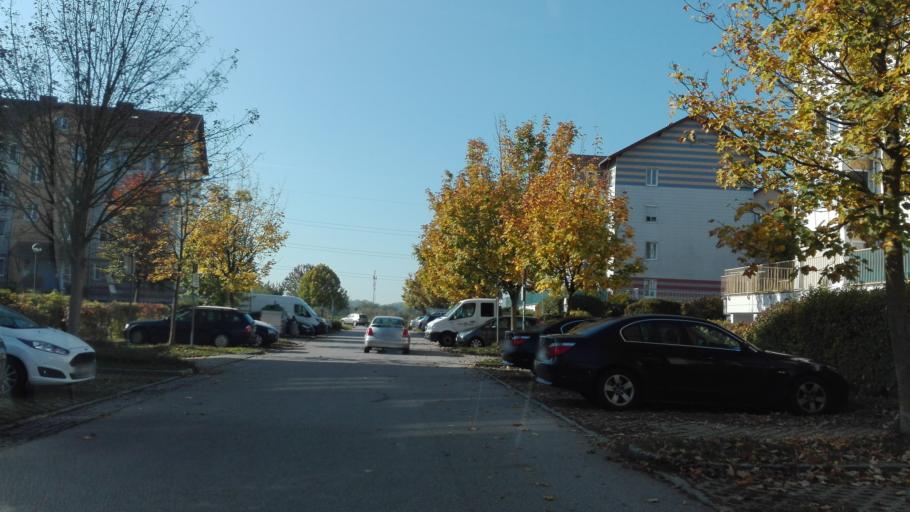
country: AT
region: Upper Austria
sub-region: Politischer Bezirk Linz-Land
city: Leonding
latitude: 48.2588
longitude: 14.2516
